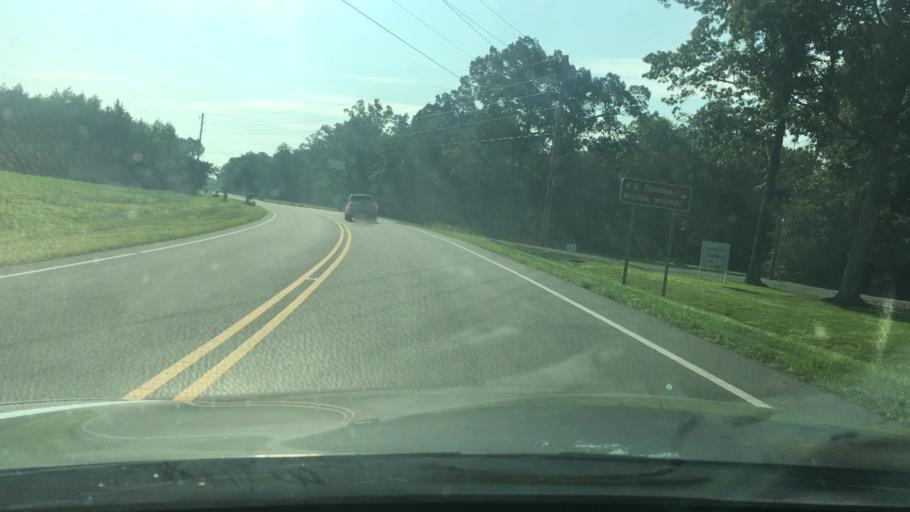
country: US
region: North Carolina
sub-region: Caswell County
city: Yanceyville
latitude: 36.2813
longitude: -79.3615
